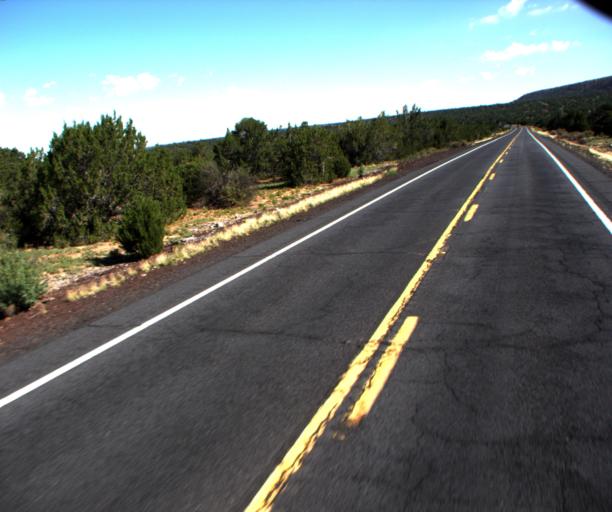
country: US
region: Arizona
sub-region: Coconino County
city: Williams
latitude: 35.4503
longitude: -112.1710
